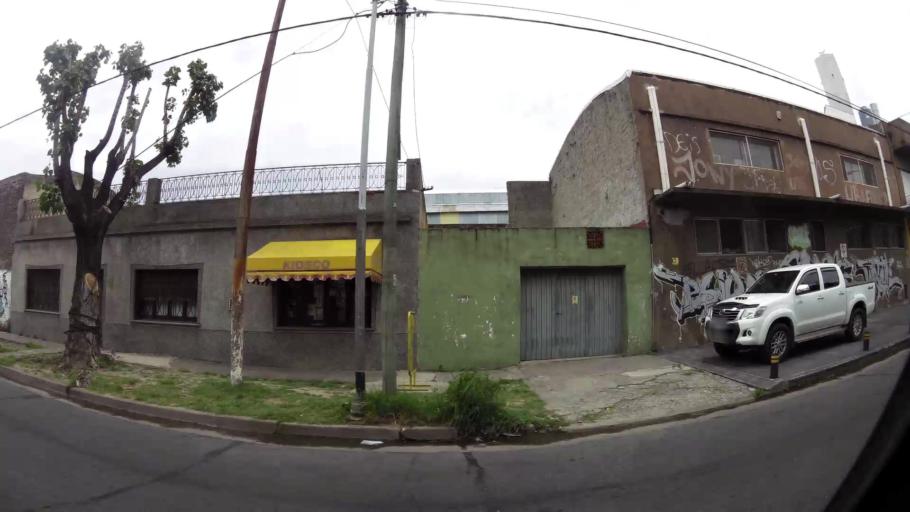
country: AR
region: Buenos Aires
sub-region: Partido de Avellaneda
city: Avellaneda
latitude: -34.6883
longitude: -58.3664
